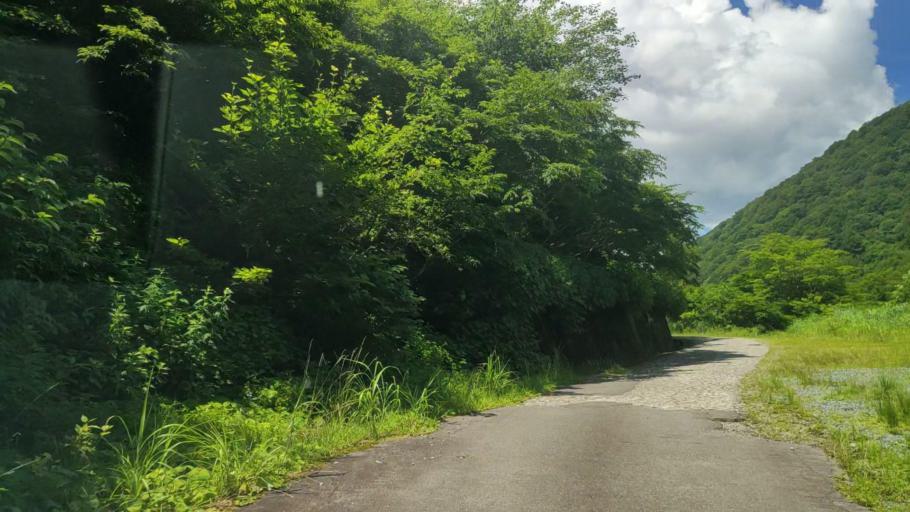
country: JP
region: Fukui
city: Ono
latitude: 35.7820
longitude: 136.5143
